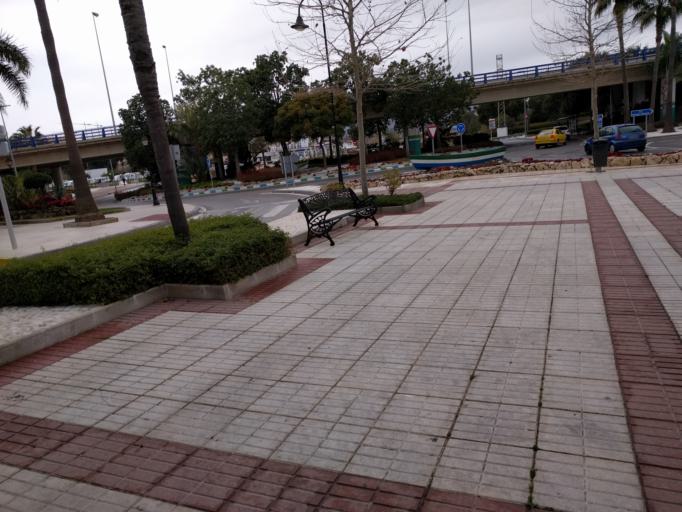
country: ES
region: Andalusia
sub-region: Provincia de Malaga
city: Fuengirola
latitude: 36.5050
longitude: -4.6800
